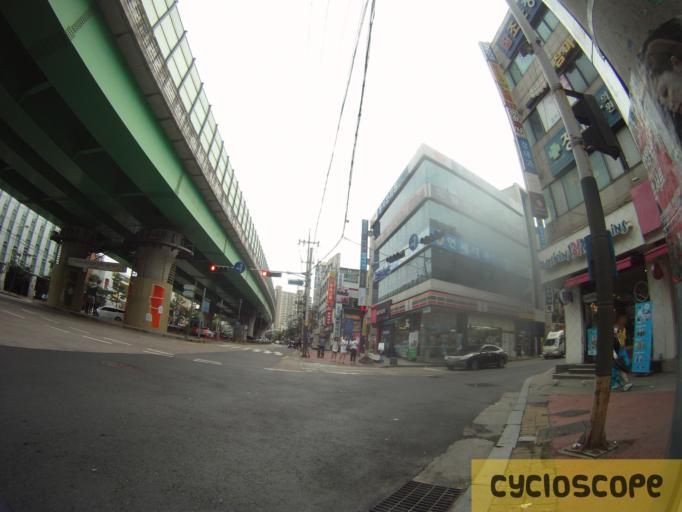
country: KR
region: Gyeonggi-do
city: Suwon-si
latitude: 37.2981
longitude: 126.9712
